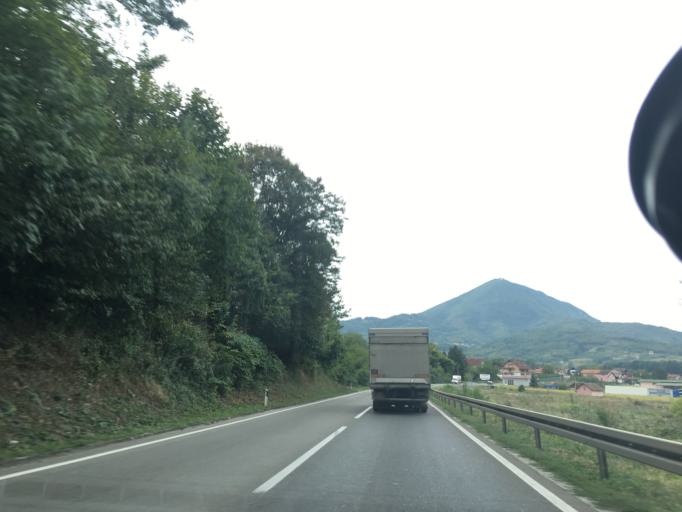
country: RS
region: Central Serbia
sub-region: Moravicki Okrug
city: Cacak
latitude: 43.8989
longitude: 20.2702
